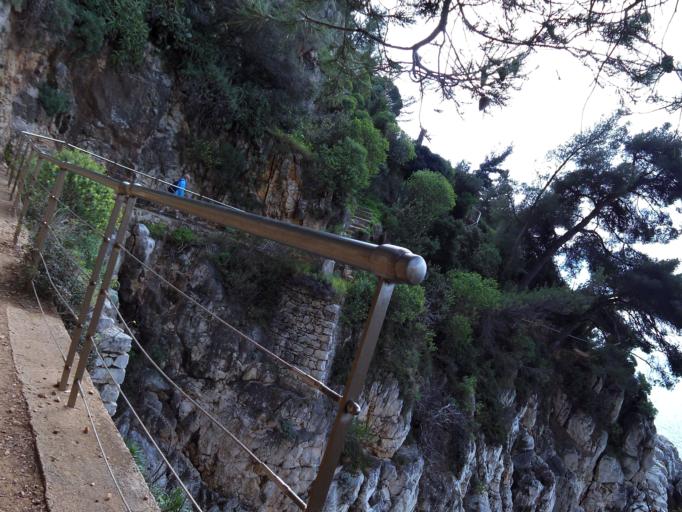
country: FR
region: Provence-Alpes-Cote d'Azur
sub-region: Departement des Alpes-Maritimes
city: Saint-Jean-Cap-Ferrat
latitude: 43.6835
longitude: 7.3246
